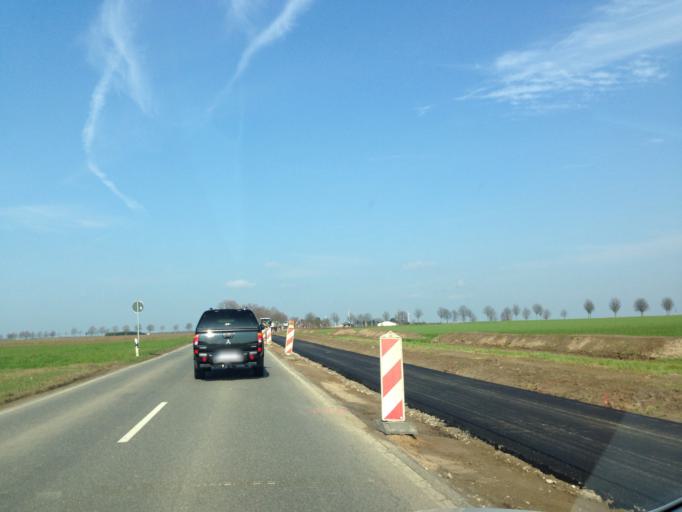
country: DE
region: North Rhine-Westphalia
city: Huckelhoven
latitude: 51.0885
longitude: 6.2455
